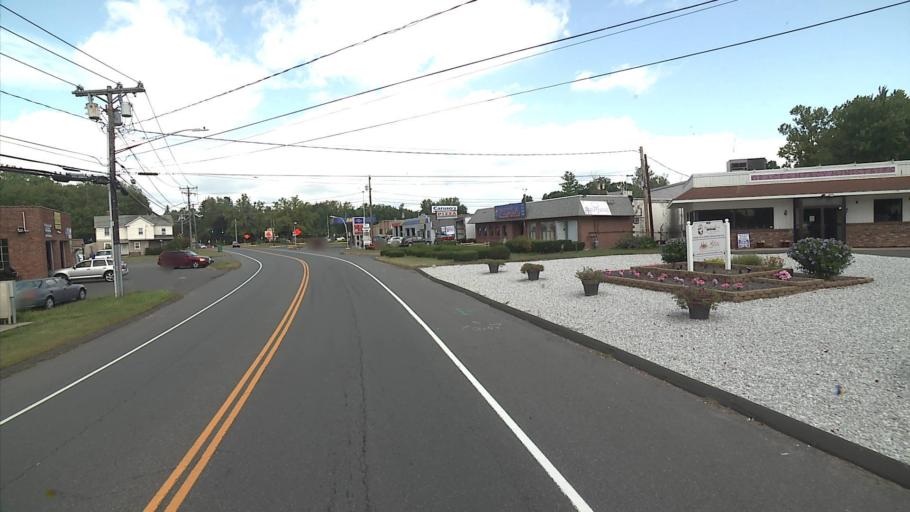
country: US
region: Connecticut
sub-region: Hartford County
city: Blue Hills
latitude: 41.8347
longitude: -72.7374
